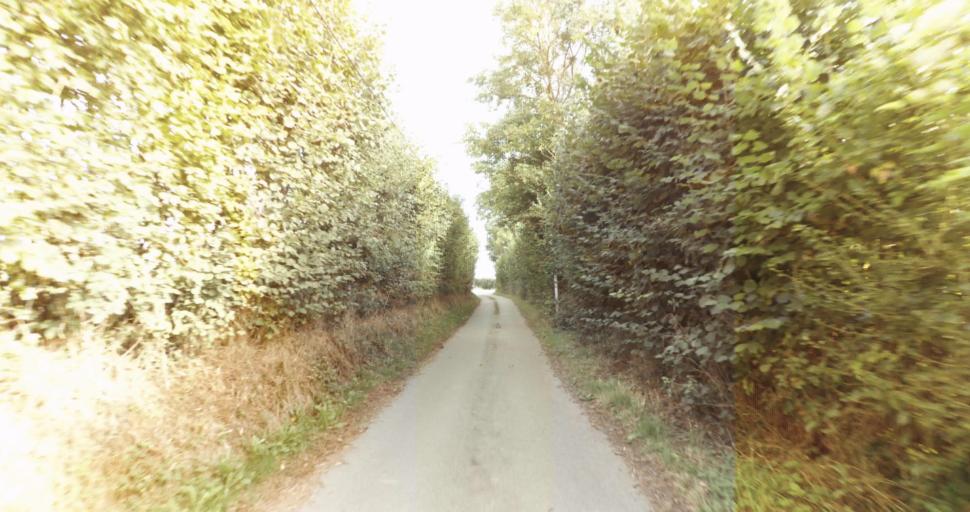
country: FR
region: Lower Normandy
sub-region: Departement de l'Orne
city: Gace
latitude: 48.6998
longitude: 0.3303
